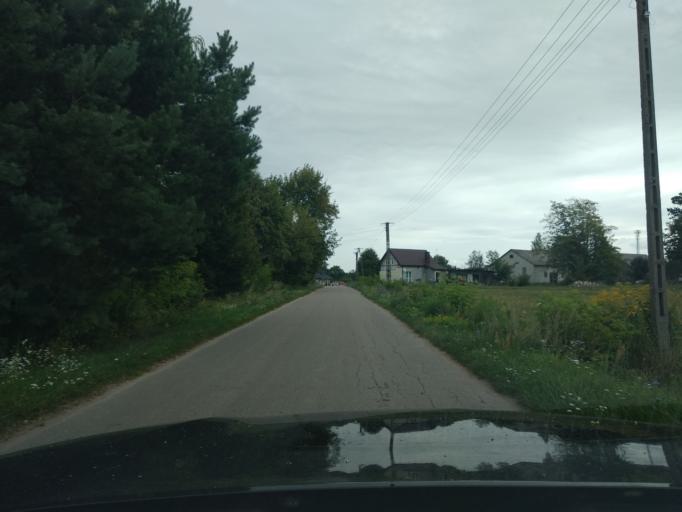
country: PL
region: Masovian Voivodeship
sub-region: Powiat pultuski
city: Obryte
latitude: 52.7536
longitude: 21.2072
